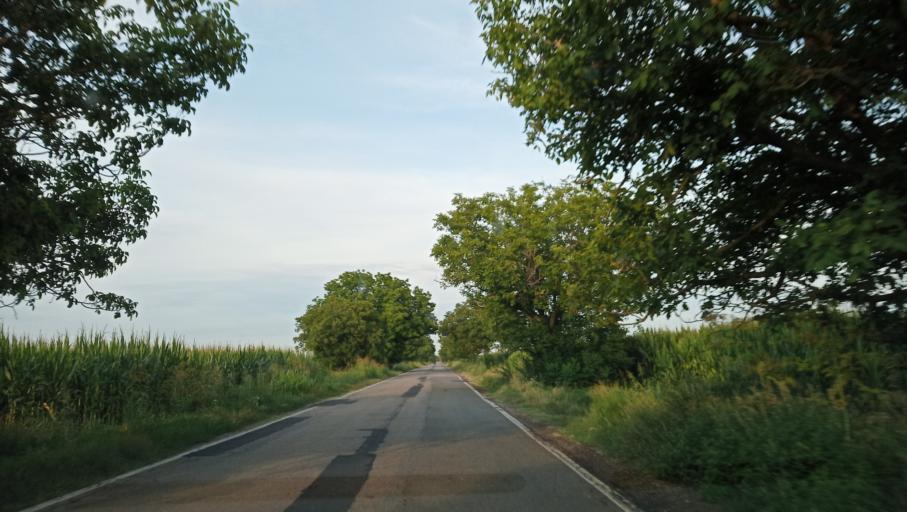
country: RO
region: Giurgiu
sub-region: Comuna Greaca
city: Greaca
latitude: 44.1044
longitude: 26.2986
